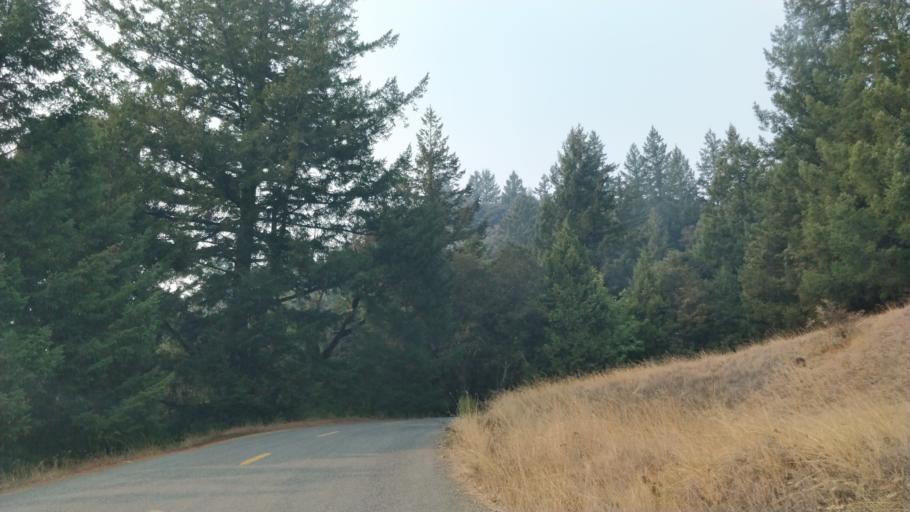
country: US
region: California
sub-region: Humboldt County
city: Rio Dell
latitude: 40.2475
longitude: -124.1224
